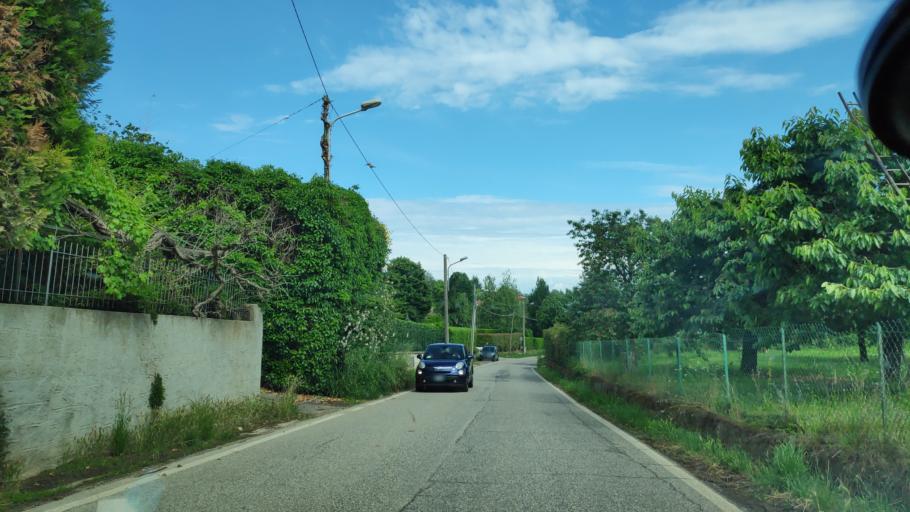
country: IT
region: Piedmont
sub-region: Provincia di Torino
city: Pecetto
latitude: 45.0056
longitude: 7.7628
